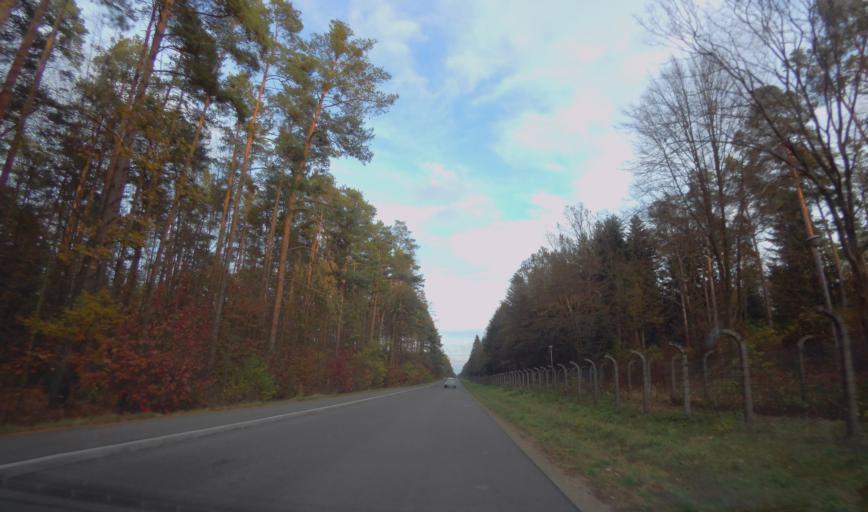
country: PL
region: Subcarpathian Voivodeship
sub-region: Powiat lezajski
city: Wola Zarczycka
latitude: 50.3286
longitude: 22.2892
